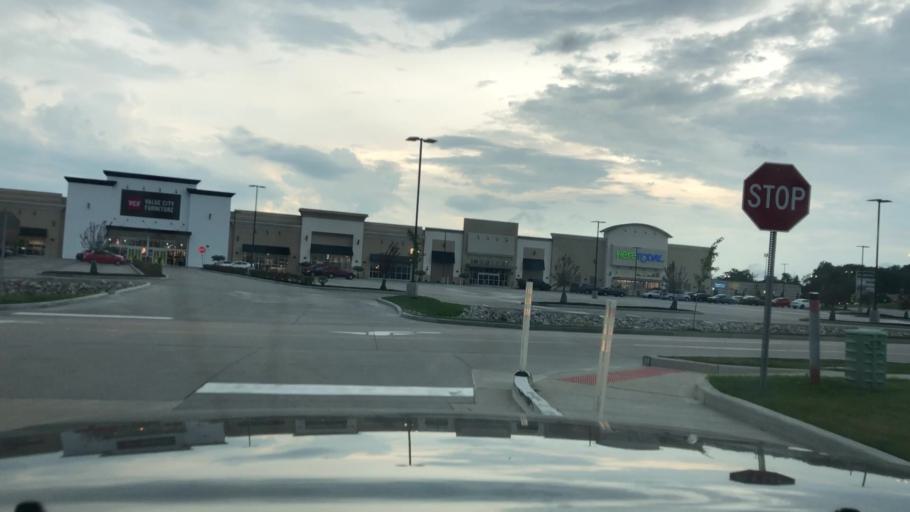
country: US
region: Missouri
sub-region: Saint Louis County
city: Saint Ann
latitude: 38.7361
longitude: -90.3982
